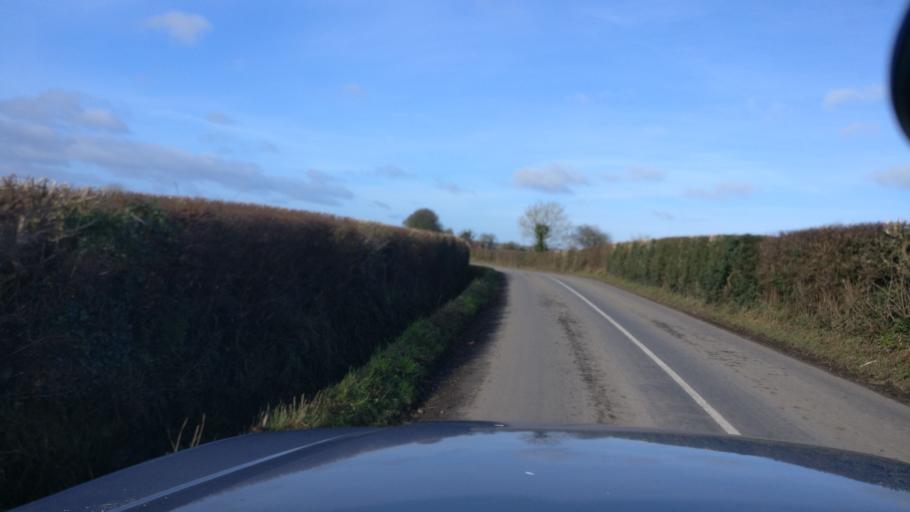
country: IE
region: Leinster
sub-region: Kilkenny
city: Castlecomer
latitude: 52.8756
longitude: -7.1613
